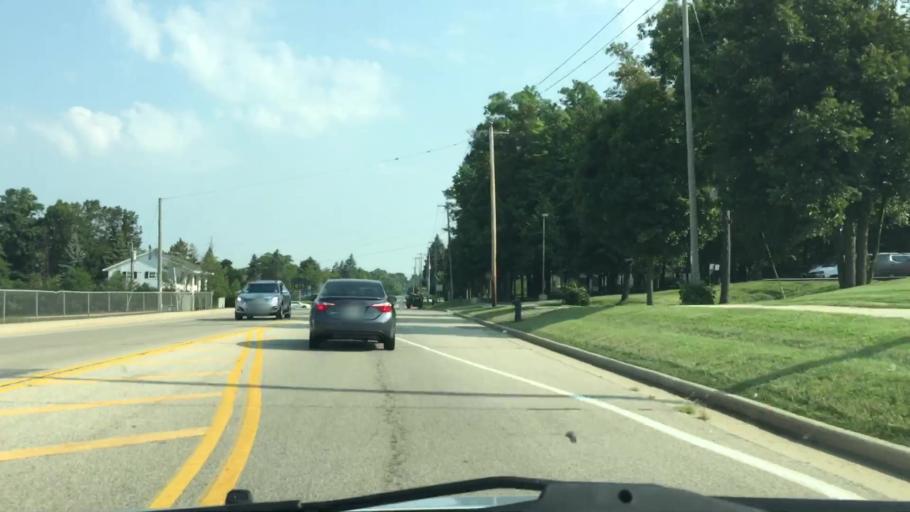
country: US
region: Wisconsin
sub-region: Waukesha County
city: Brookfield
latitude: 43.0374
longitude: -88.1467
